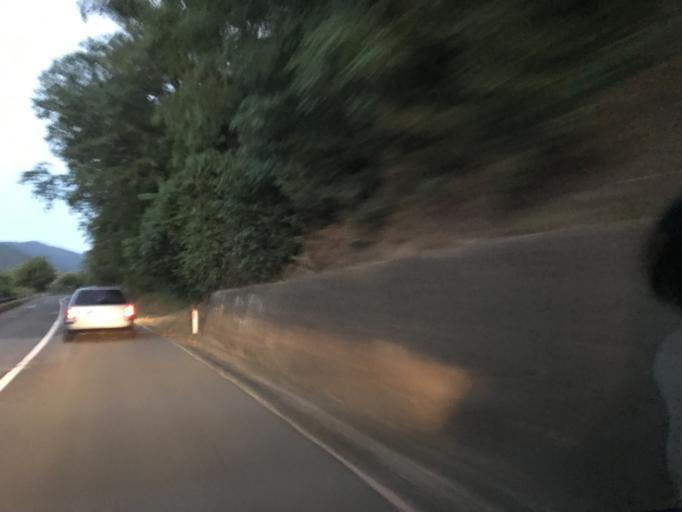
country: RO
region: Caras-Severin
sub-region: Comuna Berzasca
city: Liubcova
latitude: 44.6404
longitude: 21.9169
